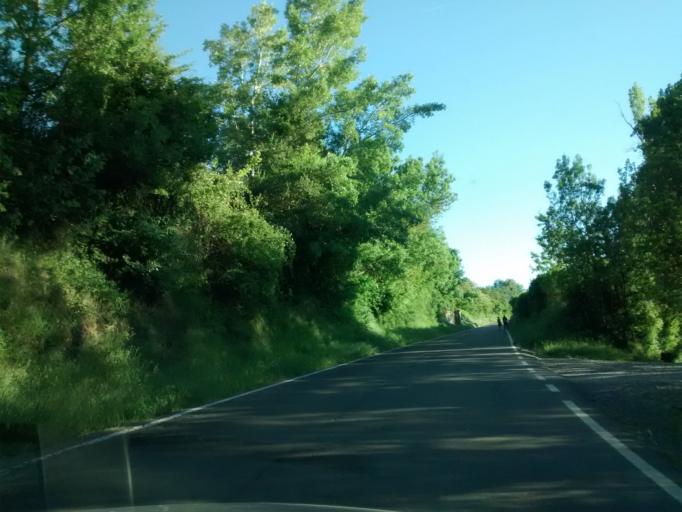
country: ES
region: Aragon
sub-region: Provincia de Huesca
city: Jaca
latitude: 42.5773
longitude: -0.5541
